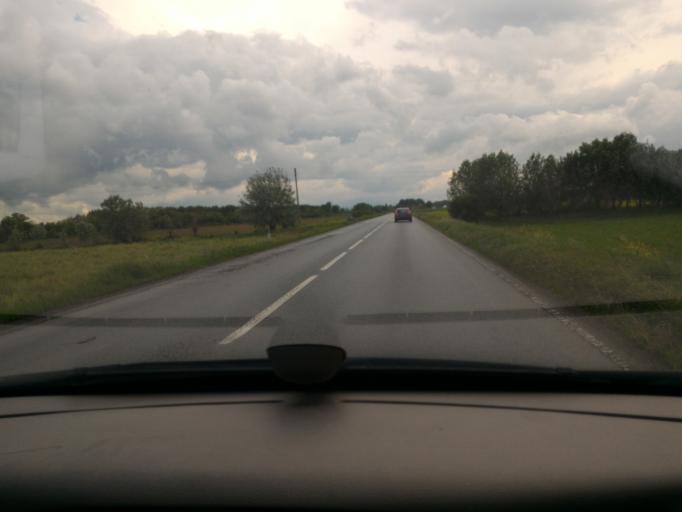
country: IT
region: Piedmont
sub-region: Provincia di Cuneo
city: Savigliano
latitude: 44.6305
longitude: 7.6657
